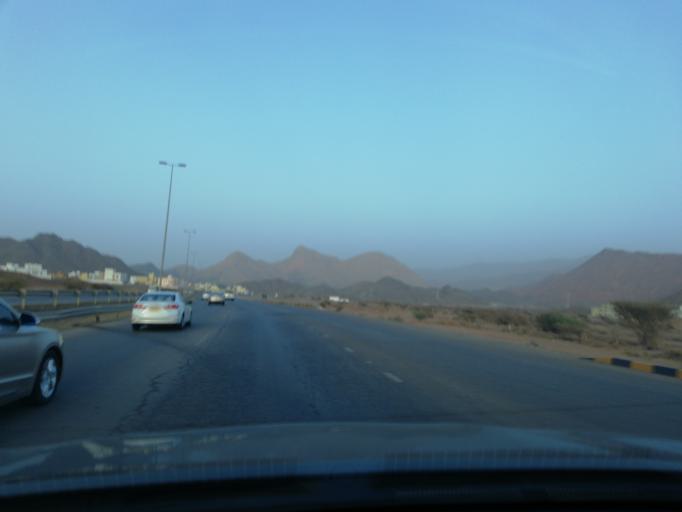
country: OM
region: Muhafazat ad Dakhiliyah
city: Bidbid
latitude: 23.4585
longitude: 58.1729
